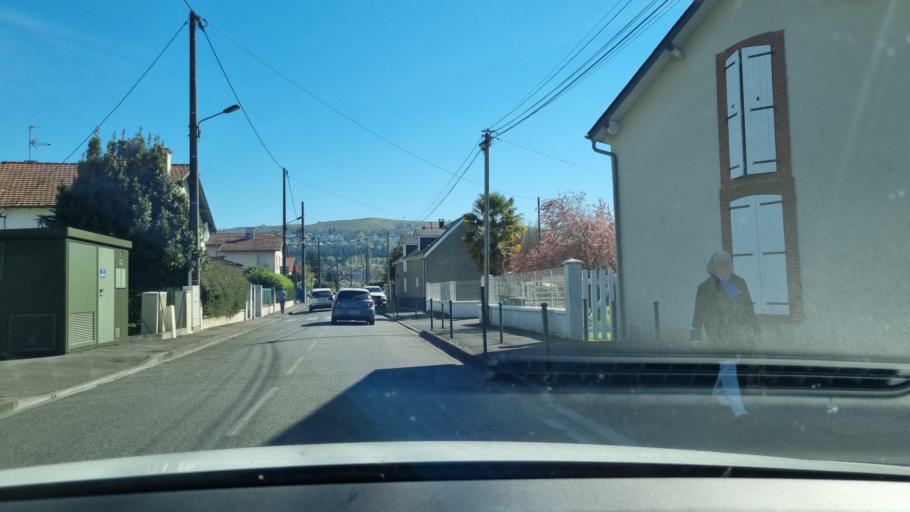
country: FR
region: Midi-Pyrenees
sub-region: Departement des Hautes-Pyrenees
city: Lourdes
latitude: 43.1019
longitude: -0.0402
